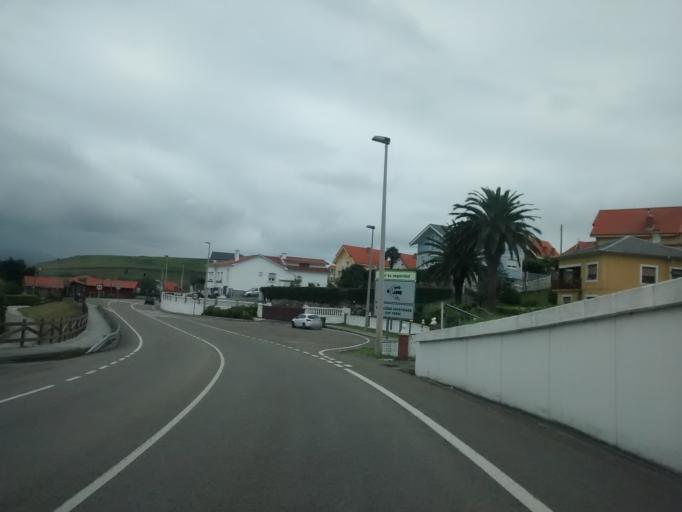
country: ES
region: Cantabria
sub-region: Provincia de Cantabria
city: Suances
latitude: 43.4146
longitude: -4.0398
